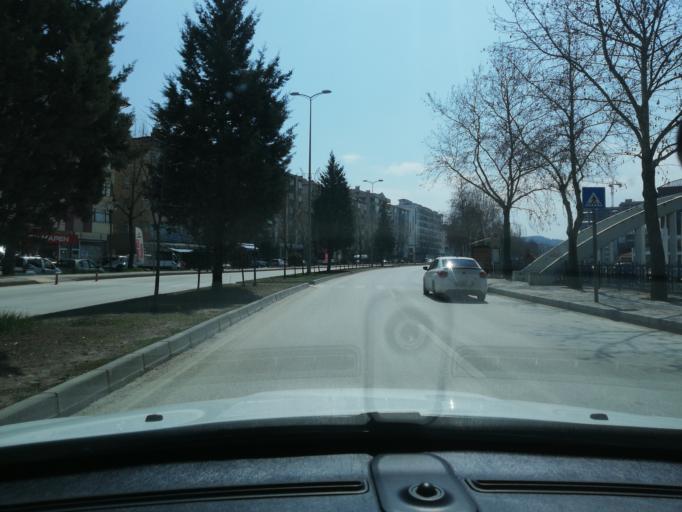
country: TR
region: Kastamonu
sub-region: Cide
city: Kastamonu
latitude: 41.3961
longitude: 33.7818
